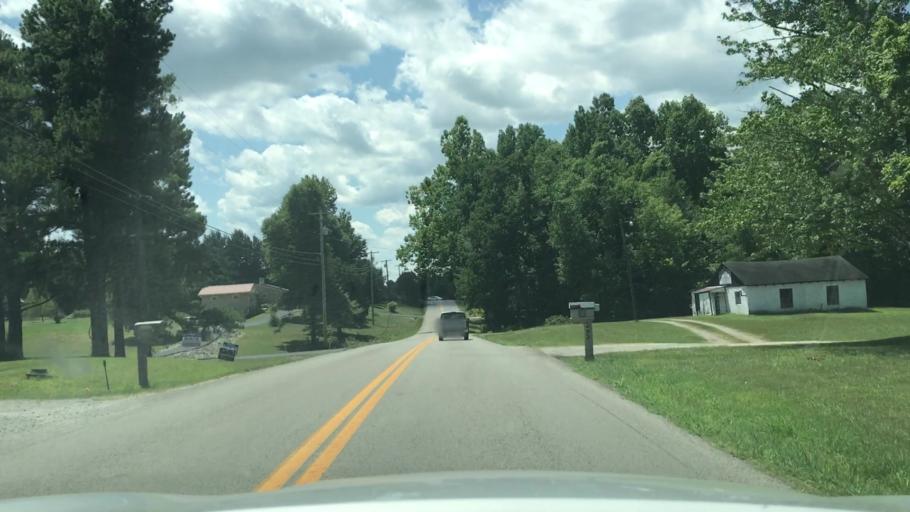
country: US
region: Kentucky
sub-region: Muhlenberg County
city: Greenville
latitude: 37.1955
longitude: -87.2124
